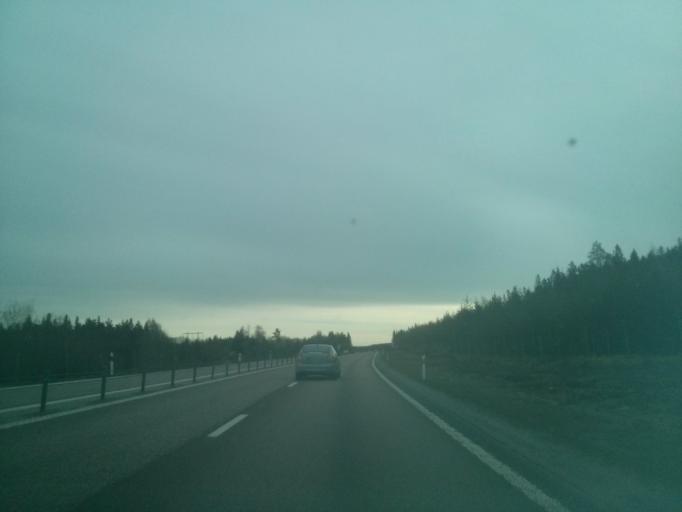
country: SE
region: Vaesternorrland
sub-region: Haernoesands Kommun
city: Haernoesand
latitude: 62.6072
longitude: 17.8247
